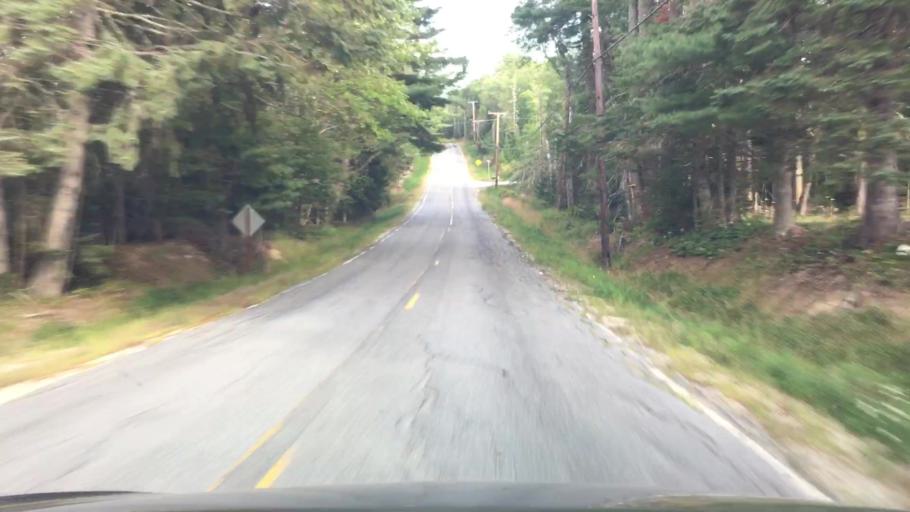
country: US
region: Maine
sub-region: Hancock County
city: Surry
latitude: 44.4937
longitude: -68.5170
